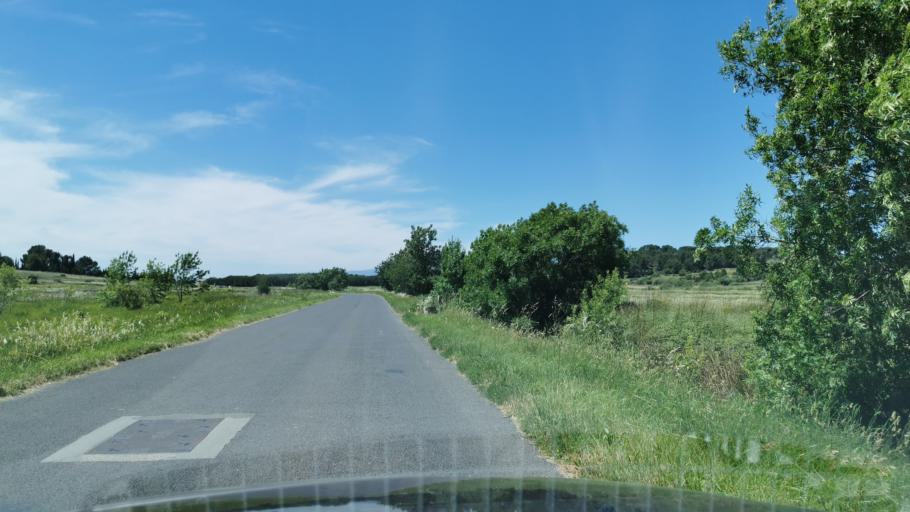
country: FR
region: Languedoc-Roussillon
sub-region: Departement de l'Aude
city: Marcorignan
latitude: 43.2158
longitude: 2.9245
